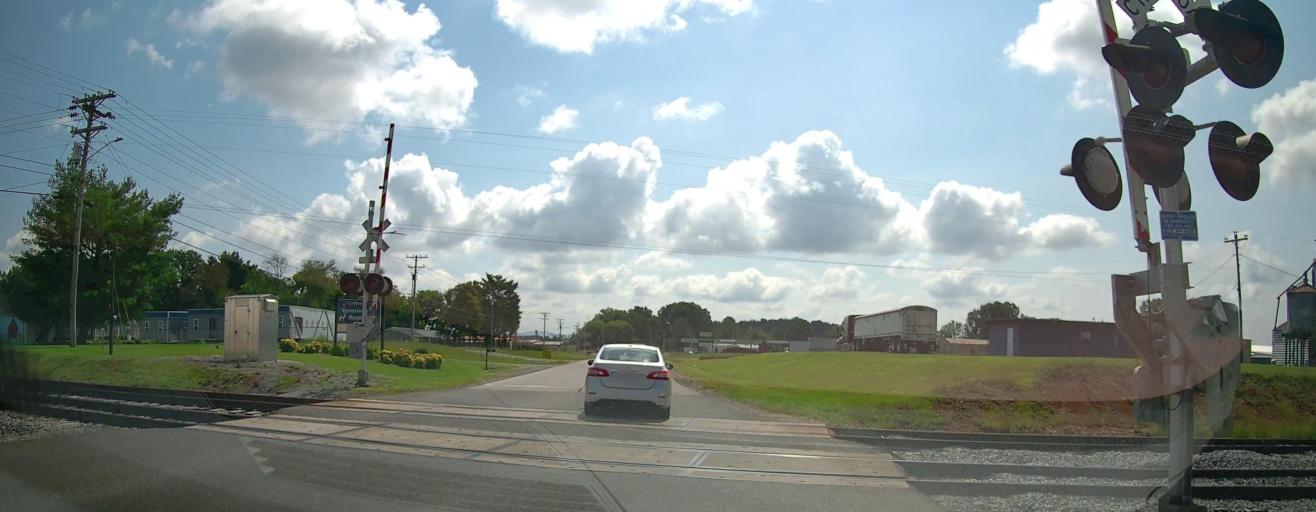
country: US
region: Tennessee
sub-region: Coffee County
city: Manchester
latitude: 35.4962
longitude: -86.0738
